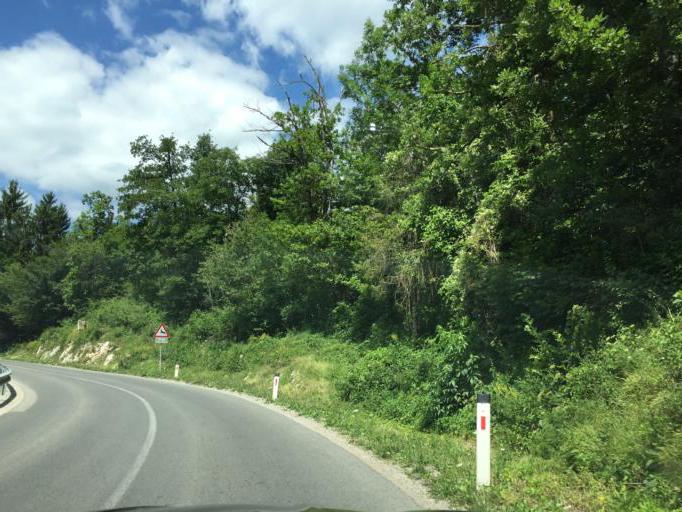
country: SI
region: Postojna
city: Postojna
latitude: 45.7990
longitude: 14.1773
